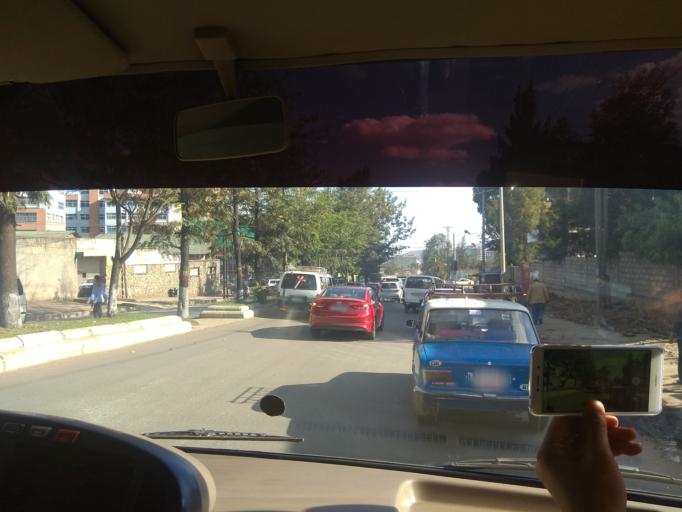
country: ET
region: Adis Abeba
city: Addis Ababa
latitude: 9.0174
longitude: 38.7463
